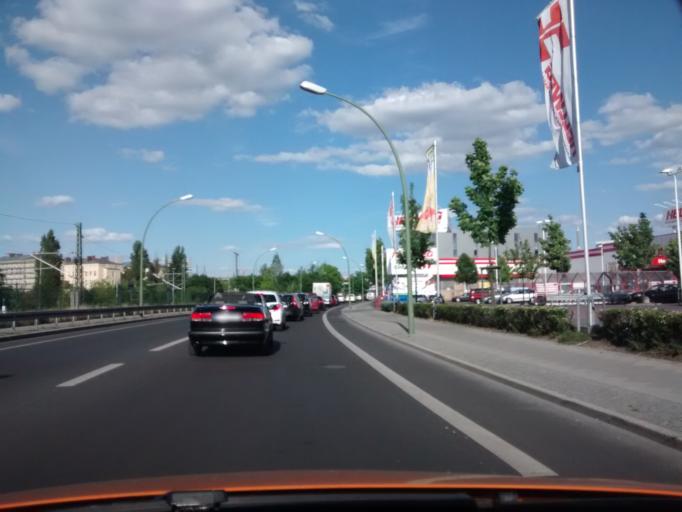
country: DE
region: Berlin
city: Wedding Bezirk
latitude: 52.5367
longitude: 13.3534
